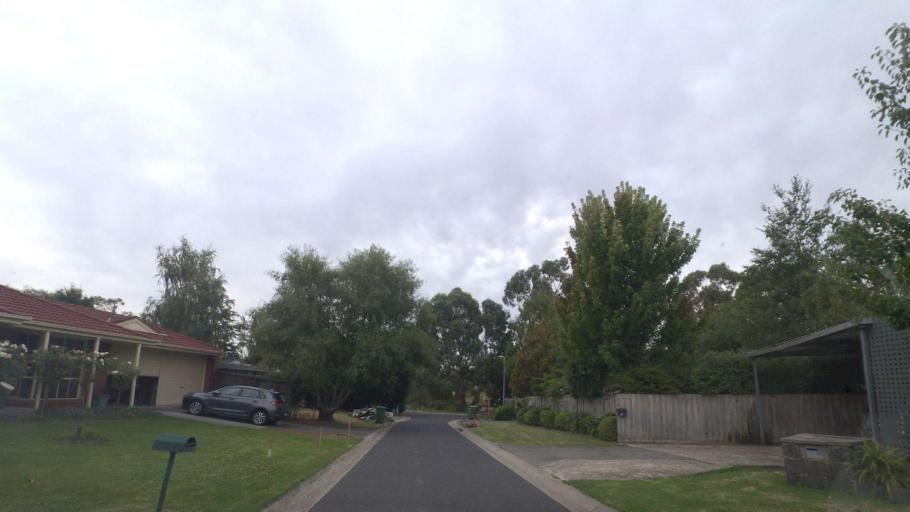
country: AU
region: Victoria
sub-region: Yarra Ranges
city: Kilsyth
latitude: -37.7880
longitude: 145.3373
